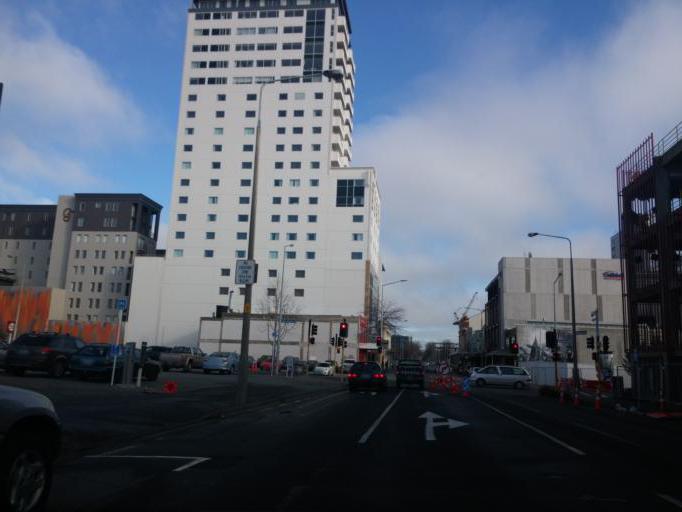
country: NZ
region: Canterbury
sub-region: Christchurch City
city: Christchurch
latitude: -43.5299
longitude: 172.6403
